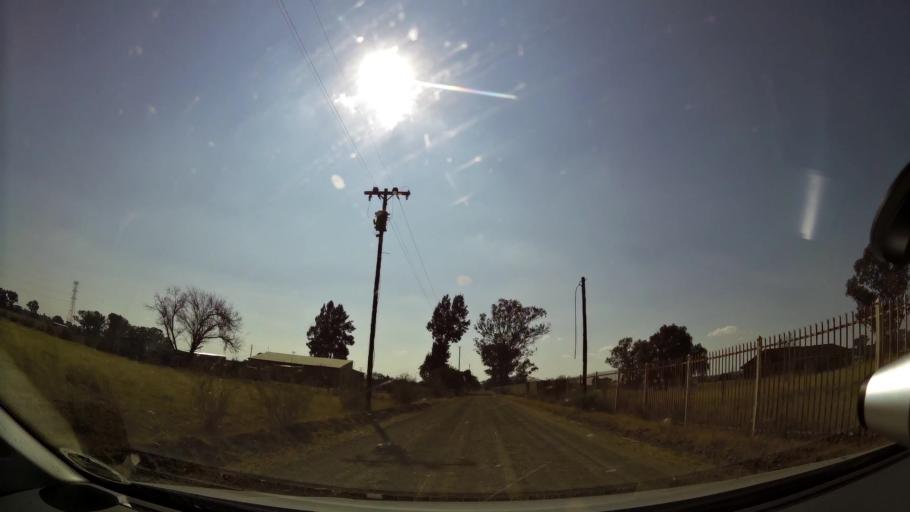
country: ZA
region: Orange Free State
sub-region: Mangaung Metropolitan Municipality
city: Bloemfontein
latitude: -29.1672
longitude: 26.3095
